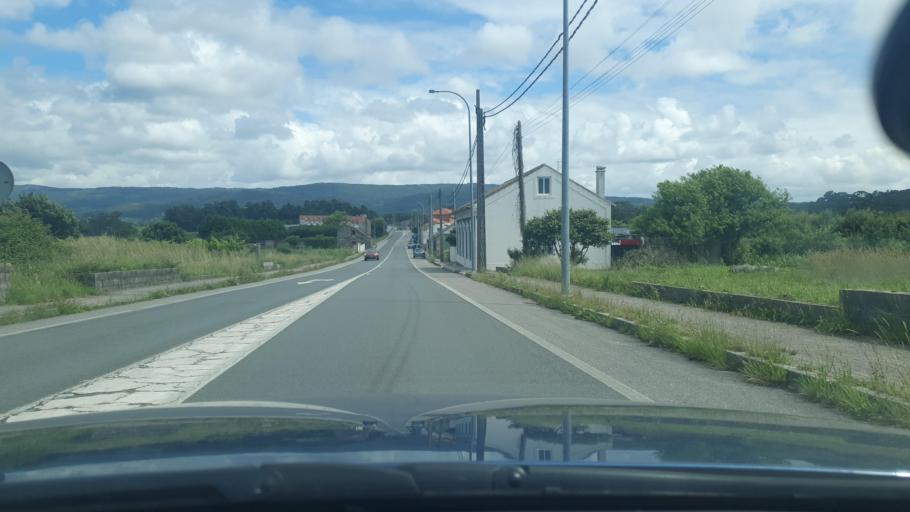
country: ES
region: Galicia
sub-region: Provincia de Pontevedra
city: Cambados
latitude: 42.5039
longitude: -8.8088
